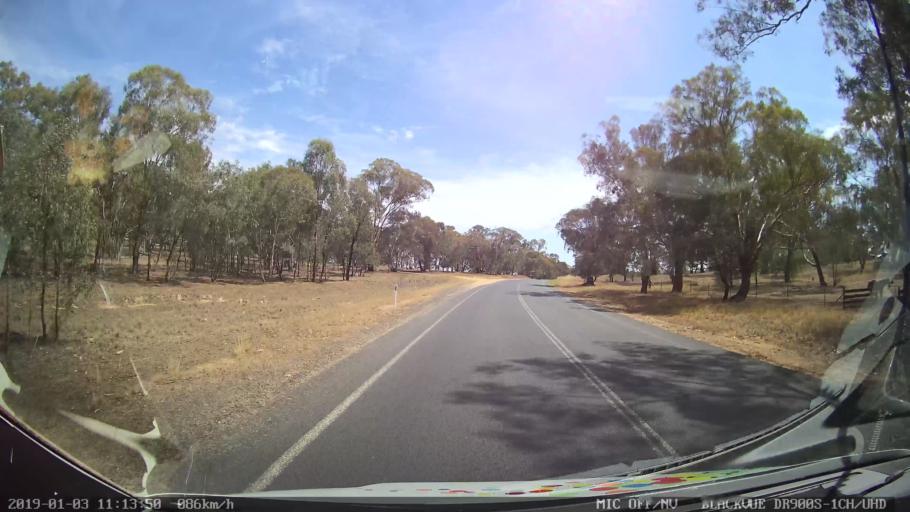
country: AU
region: New South Wales
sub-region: Young
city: Young
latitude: -34.1836
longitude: 148.2599
